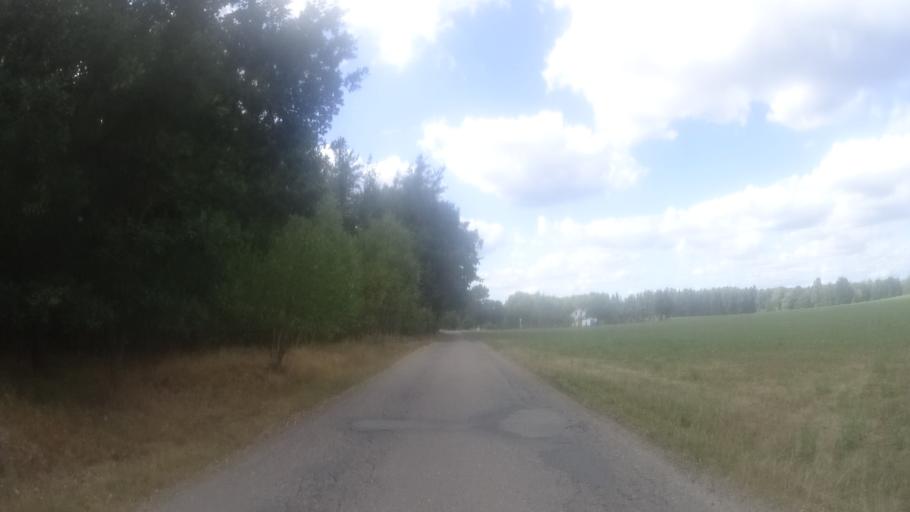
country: CZ
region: Pardubicky
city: Horni Jeleni
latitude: 50.0575
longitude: 16.1488
